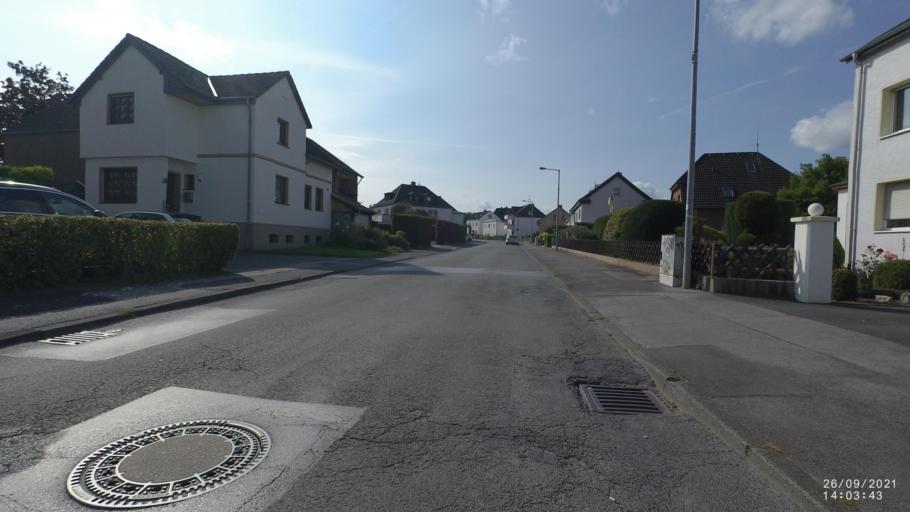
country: DE
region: North Rhine-Westphalia
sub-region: Regierungsbezirk Arnsberg
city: Frondenberg
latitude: 51.4556
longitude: 7.7546
